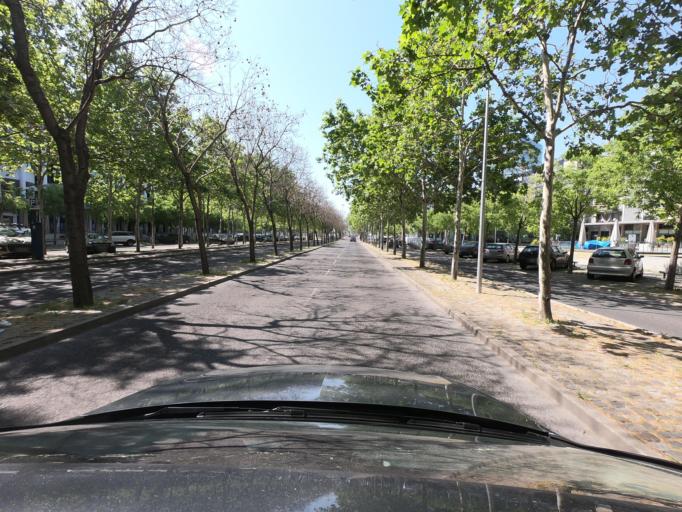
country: PT
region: Lisbon
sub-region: Loures
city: Moscavide
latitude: 38.7772
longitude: -9.0951
